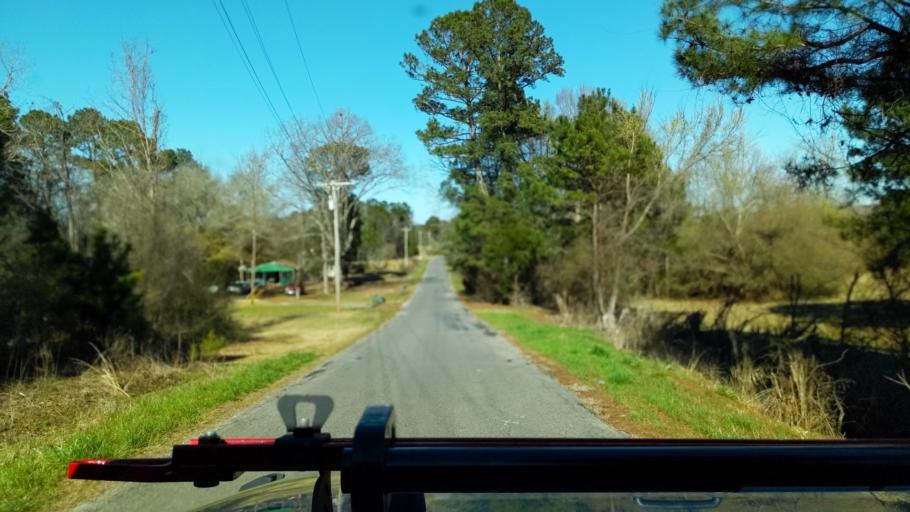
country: US
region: Alabama
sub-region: Walker County
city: Jasper
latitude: 34.0514
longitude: -87.1553
